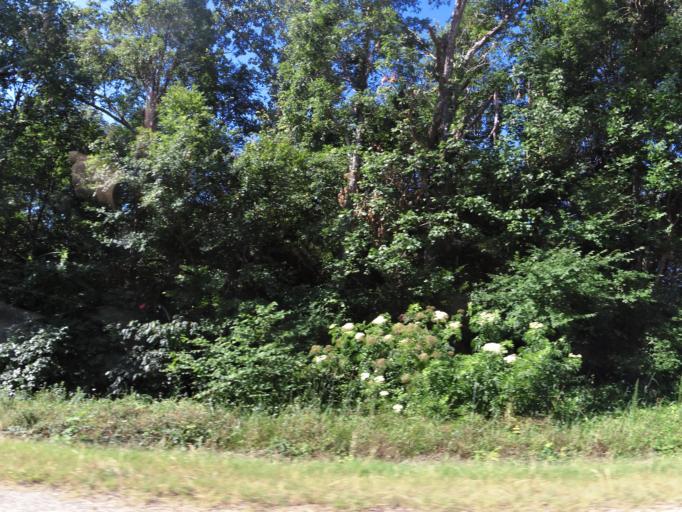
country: US
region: Arkansas
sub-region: Clay County
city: Piggott
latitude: 36.4331
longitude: -90.3092
